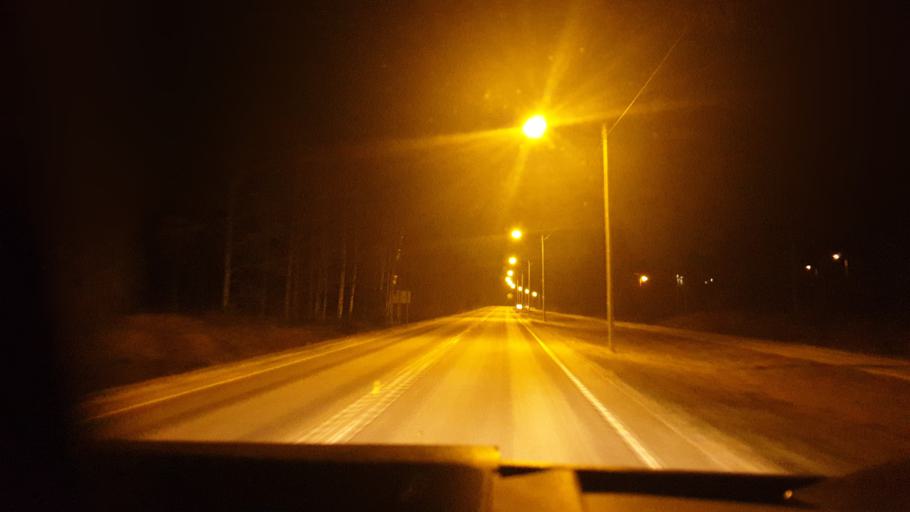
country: FI
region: Southern Ostrobothnia
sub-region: Kuusiokunnat
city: Alavus
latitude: 62.5963
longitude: 23.6437
